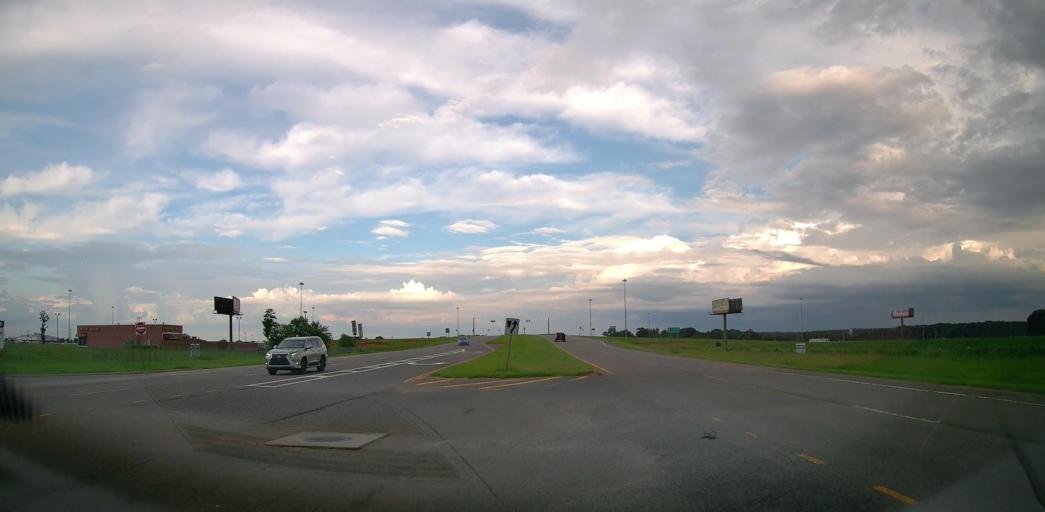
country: US
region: Georgia
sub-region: Houston County
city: Perry
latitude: 32.4329
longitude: -83.7609
